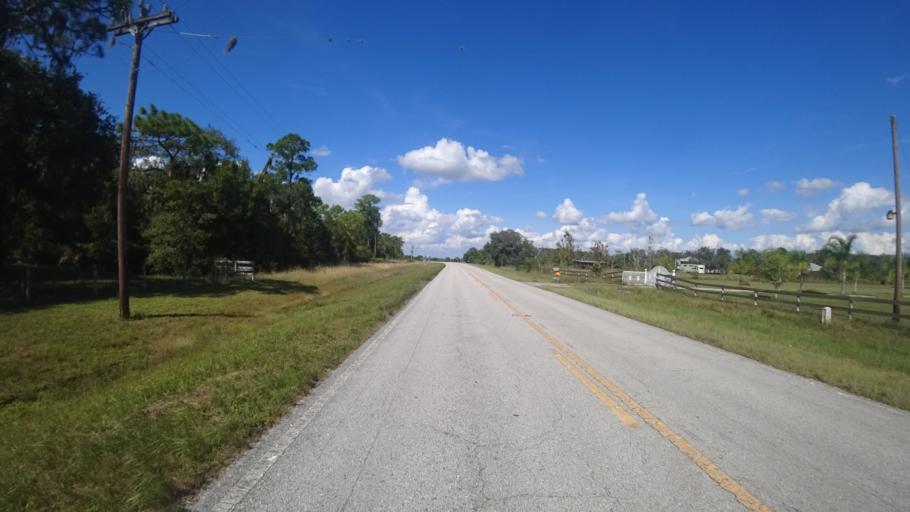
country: US
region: Florida
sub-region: Sarasota County
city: The Meadows
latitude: 27.4653
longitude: -82.3032
